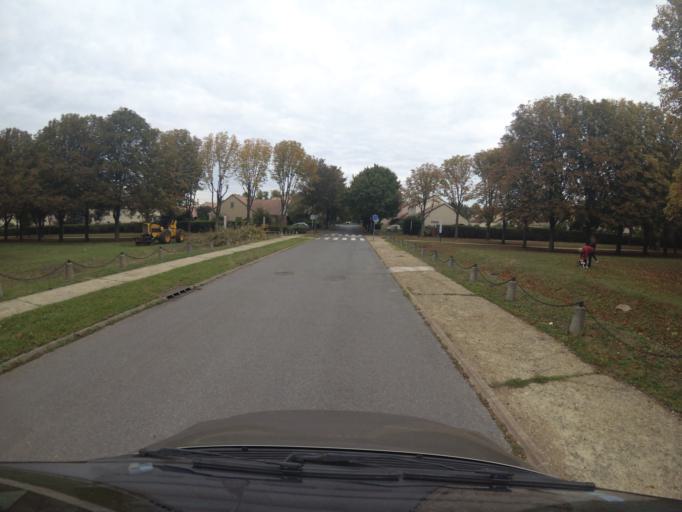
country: FR
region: Ile-de-France
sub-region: Departement de Seine-et-Marne
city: Collegien
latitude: 48.8528
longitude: 2.6723
